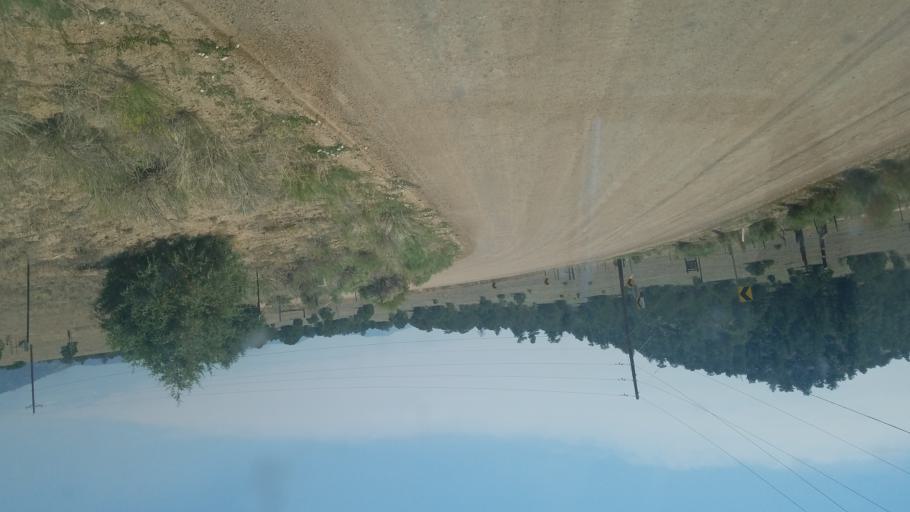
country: US
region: Colorado
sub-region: Custer County
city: Westcliffe
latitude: 38.2998
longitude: -105.4865
